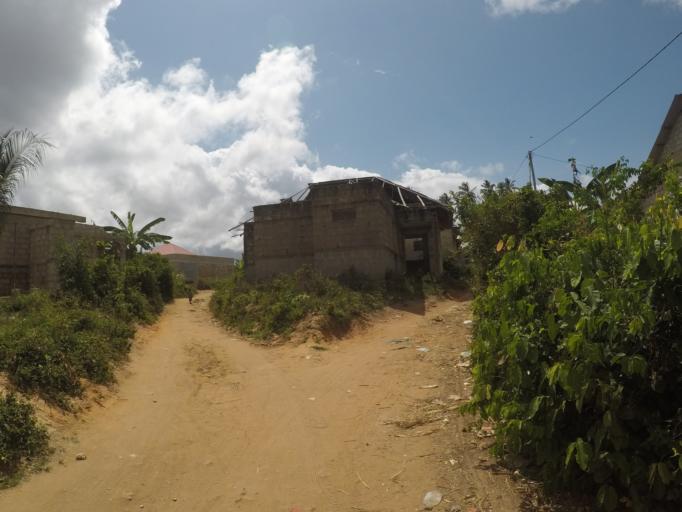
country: TZ
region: Zanzibar Urban/West
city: Zanzibar
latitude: -6.2015
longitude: 39.2370
